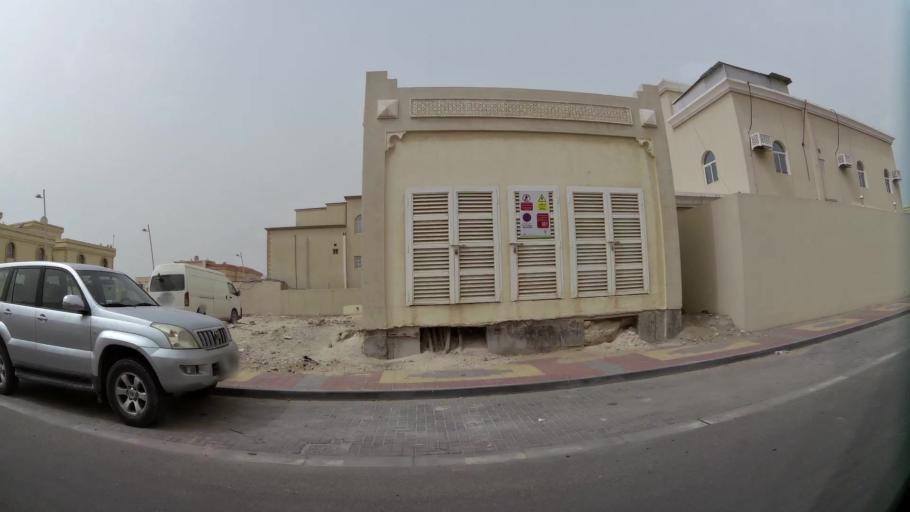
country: QA
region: Baladiyat ad Dawhah
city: Doha
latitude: 25.2311
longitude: 51.5490
